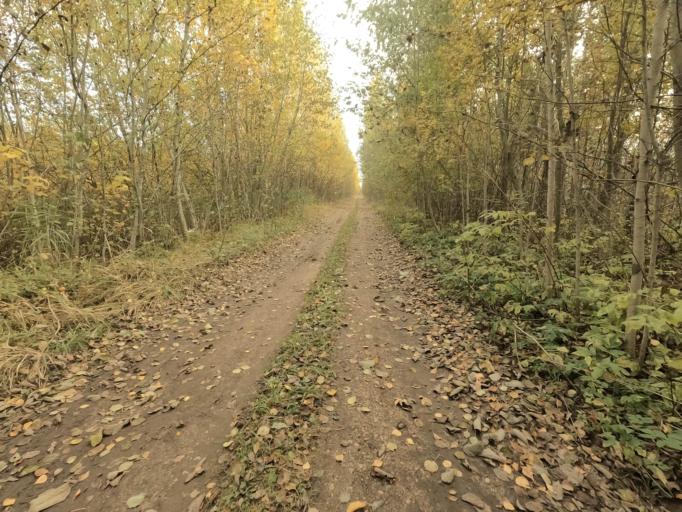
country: RU
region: Novgorod
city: Pankovka
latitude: 58.8790
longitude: 30.8550
